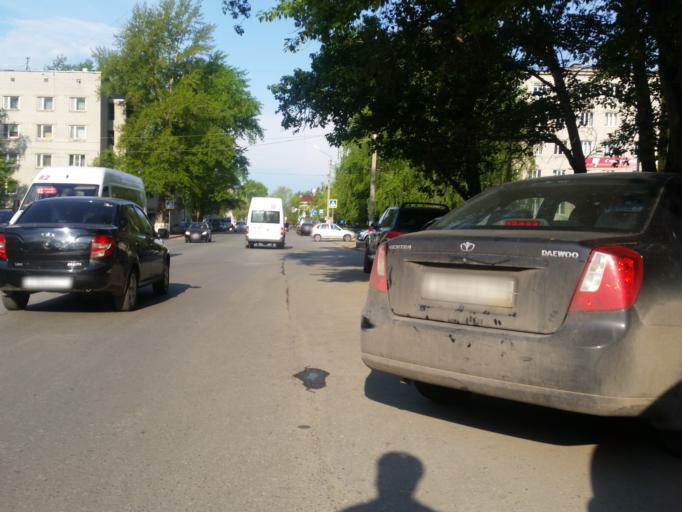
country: RU
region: Ulyanovsk
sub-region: Ulyanovskiy Rayon
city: Ulyanovsk
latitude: 54.3281
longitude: 48.3914
